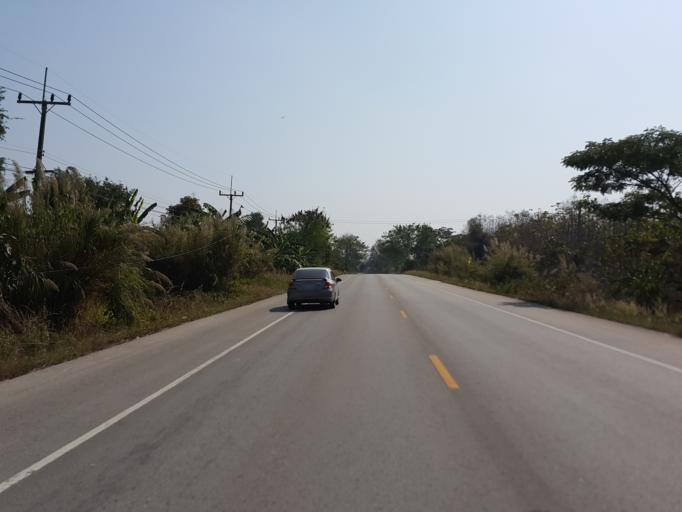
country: TH
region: Lampang
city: Wang Nuea
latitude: 18.9761
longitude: 99.6098
